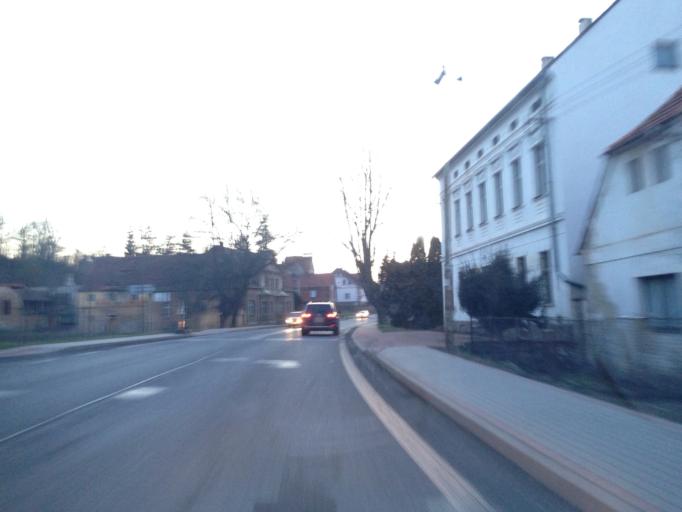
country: CZ
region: Central Bohemia
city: Jesenice
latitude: 50.1556
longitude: 13.5300
